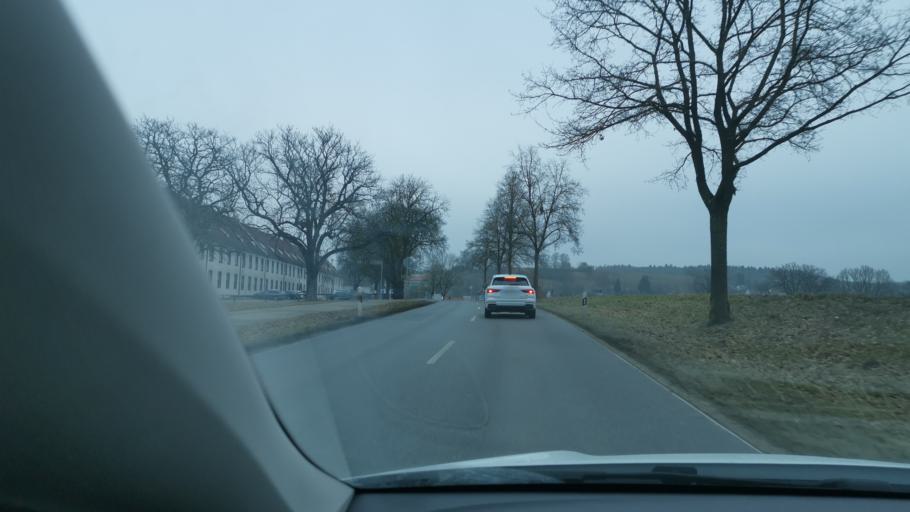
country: DE
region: Bavaria
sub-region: Swabia
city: Thierhaupten
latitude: 48.5597
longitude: 10.9115
